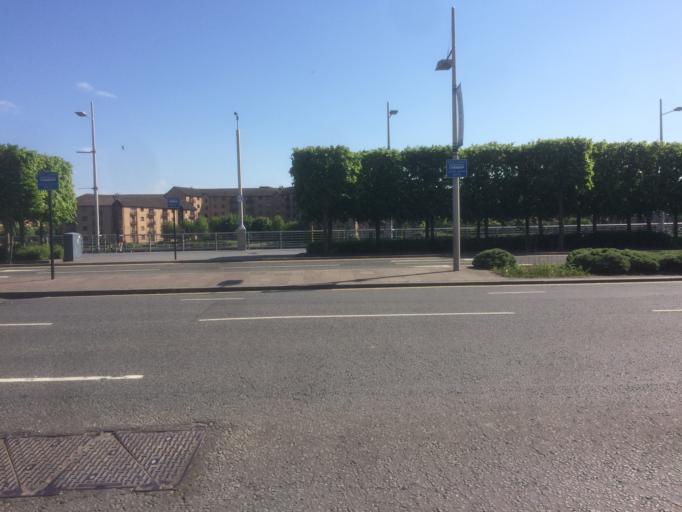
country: GB
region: Scotland
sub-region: Glasgow City
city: Glasgow
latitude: 55.8568
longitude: -4.2674
